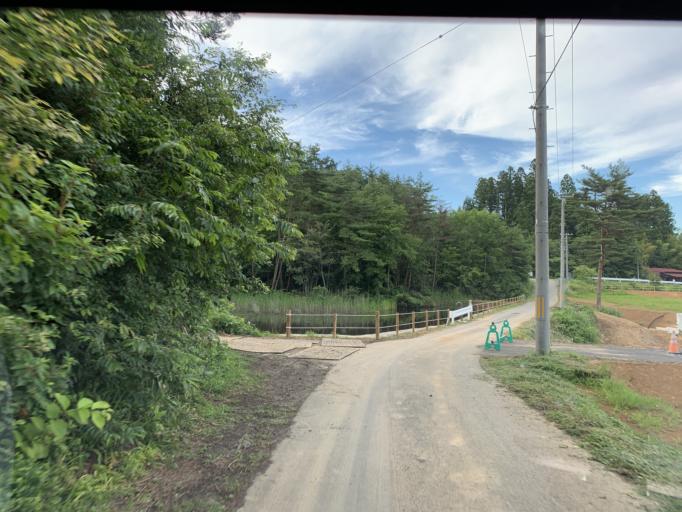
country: JP
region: Iwate
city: Ichinoseki
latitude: 38.9043
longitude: 141.0112
